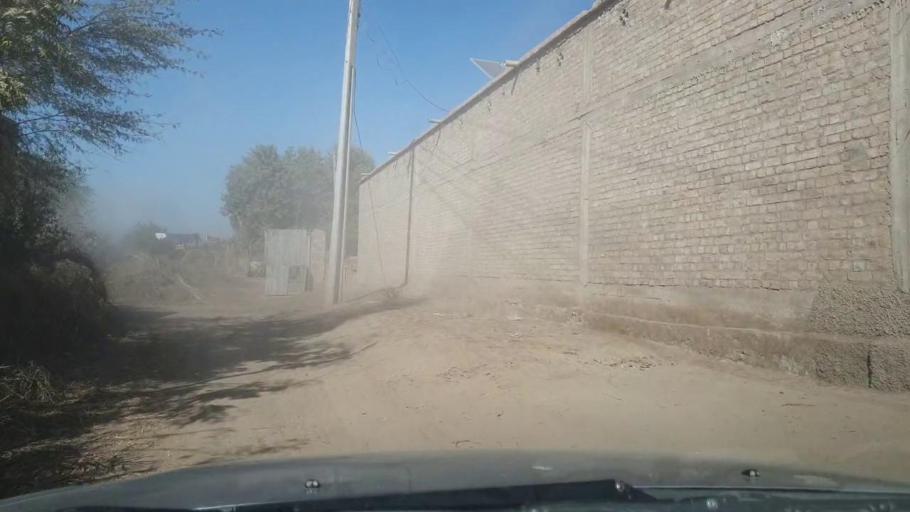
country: PK
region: Sindh
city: Ghotki
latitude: 28.0527
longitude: 69.2298
